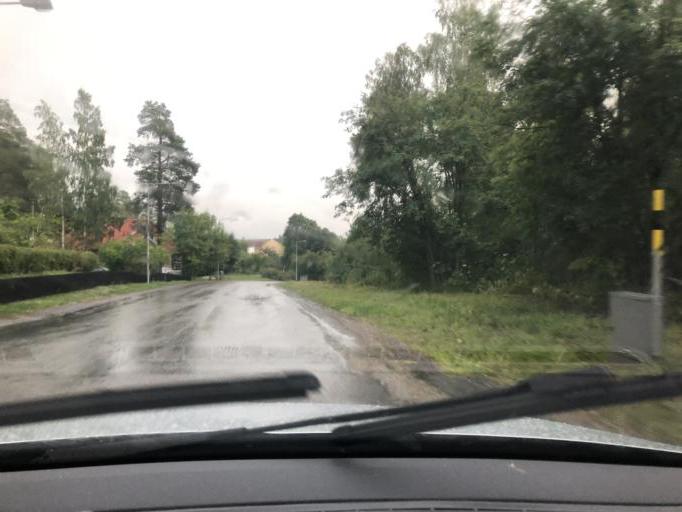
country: SE
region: Vaesternorrland
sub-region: Sundsvalls Kommun
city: Sundsvall
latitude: 62.3987
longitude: 17.3091
